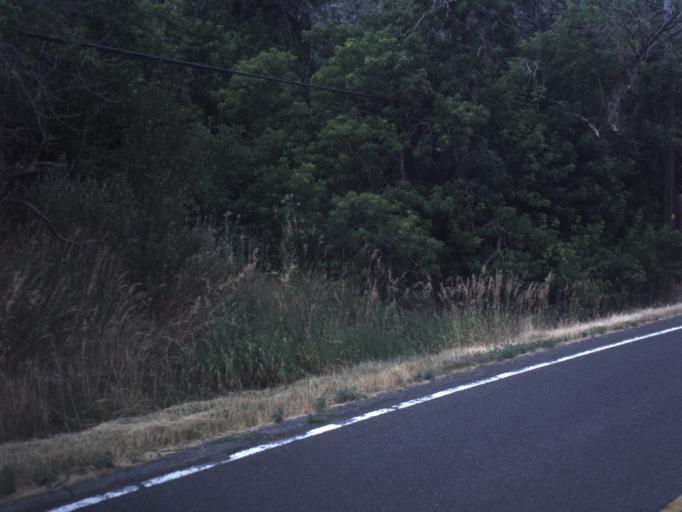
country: US
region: Utah
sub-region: Weber County
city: Washington Terrace
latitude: 41.1478
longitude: -111.9805
